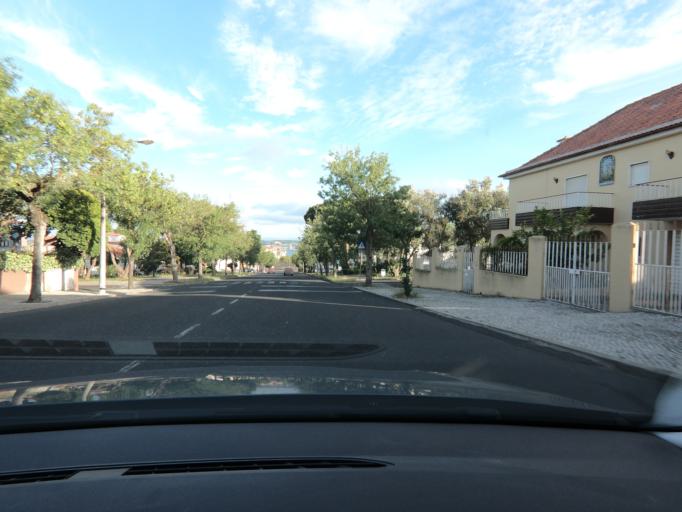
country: PT
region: Lisbon
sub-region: Oeiras
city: Alges
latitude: 38.7105
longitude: -9.2006
